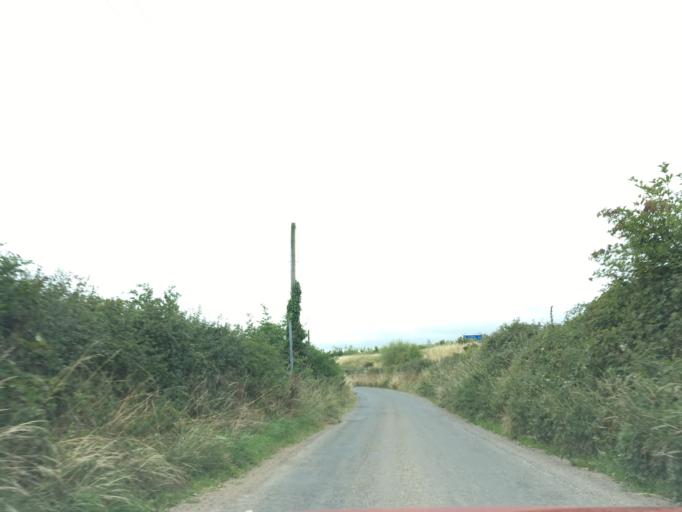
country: IE
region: Munster
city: Cashel
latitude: 52.4779
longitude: -7.9079
